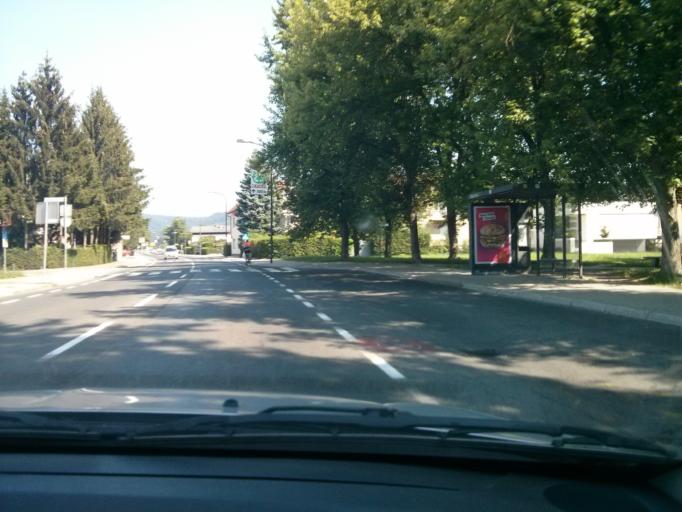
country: SI
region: Ljubljana
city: Ljubljana
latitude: 46.0742
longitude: 14.4759
